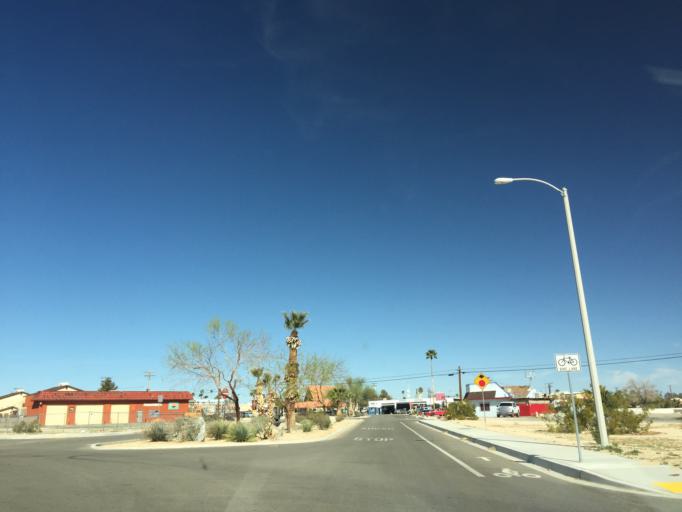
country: US
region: California
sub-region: San Bernardino County
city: Twentynine Palms
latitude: 34.1345
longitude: -116.0506
